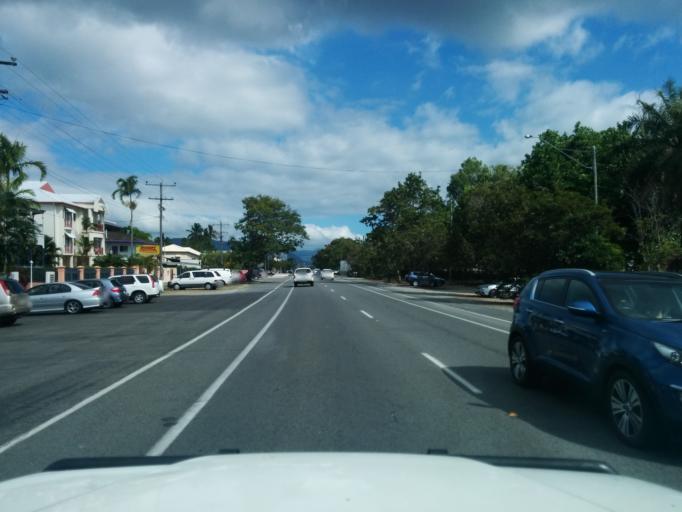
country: AU
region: Queensland
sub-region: Cairns
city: Cairns
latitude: -16.9147
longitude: 145.7644
